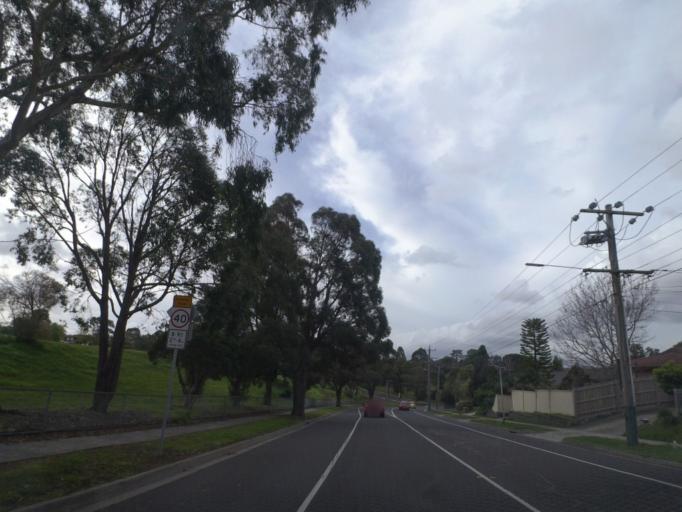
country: AU
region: Victoria
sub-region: Whitehorse
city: Vermont South
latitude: -37.8531
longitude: 145.1843
